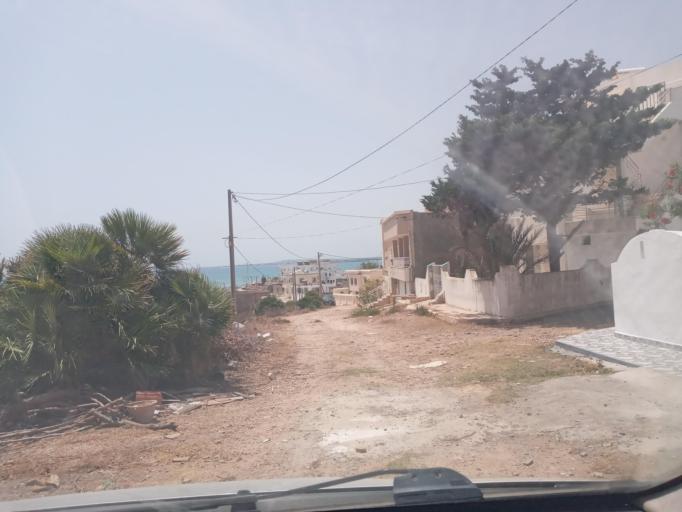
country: TN
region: Nabul
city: El Haouaria
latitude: 37.0434
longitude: 11.0615
